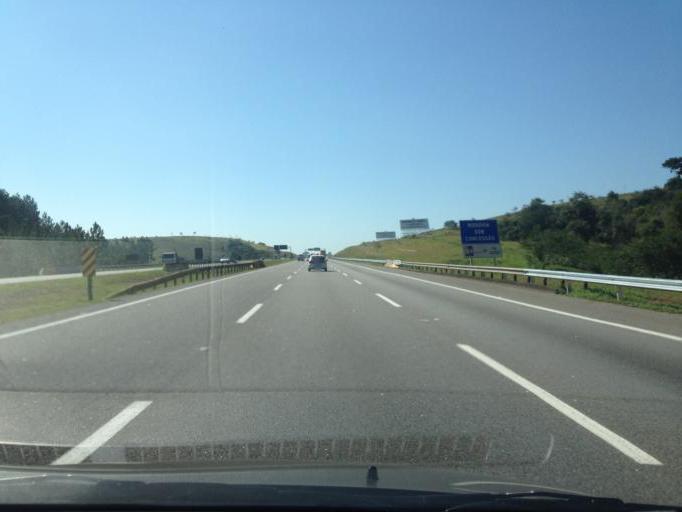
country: BR
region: Sao Paulo
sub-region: Guararema
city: Guararema
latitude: -23.3489
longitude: -46.0469
